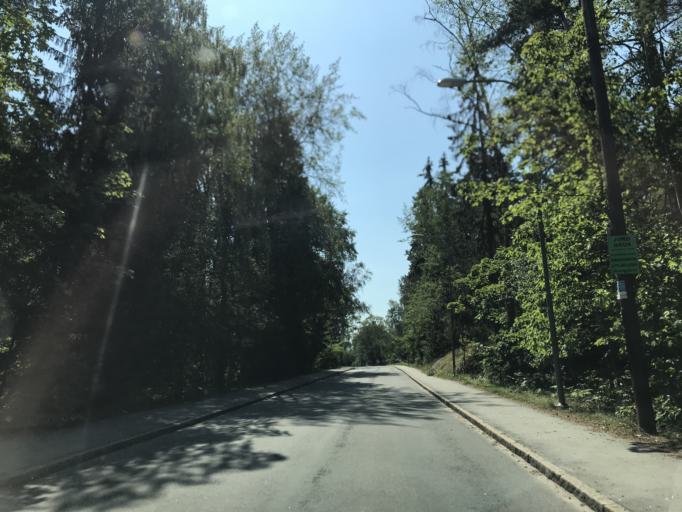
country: SE
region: Stockholm
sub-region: Stockholms Kommun
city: Bromma
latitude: 59.3274
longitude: 17.9550
